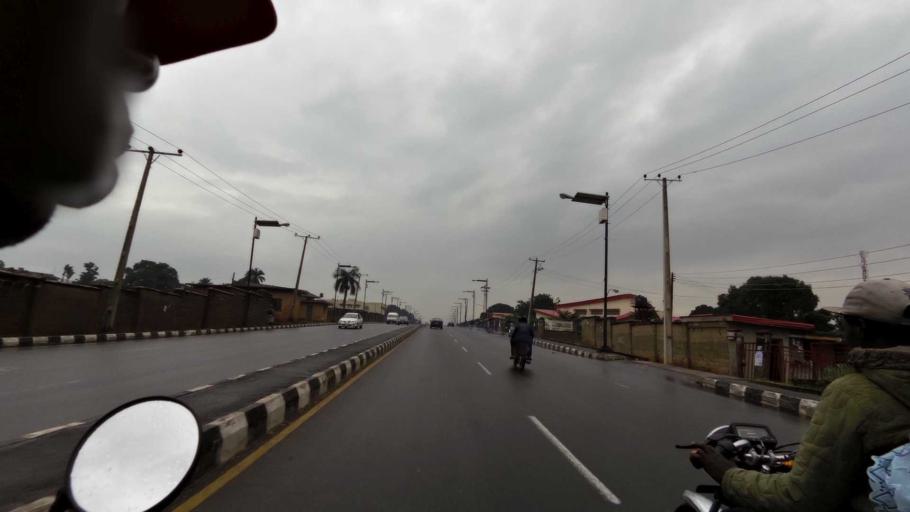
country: NG
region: Oyo
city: Ibadan
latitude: 7.3991
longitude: 3.9037
